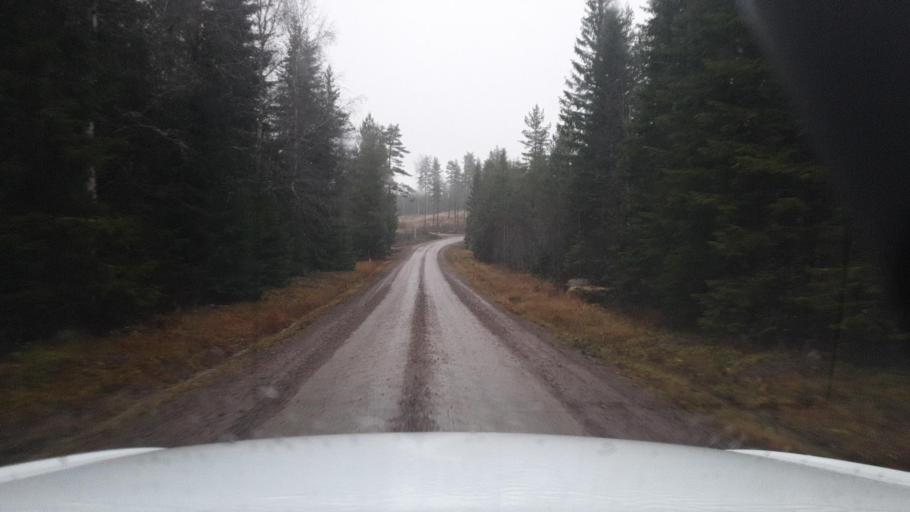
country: SE
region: Vaermland
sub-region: Arvika Kommun
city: Arvika
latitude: 59.9839
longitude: 12.6607
